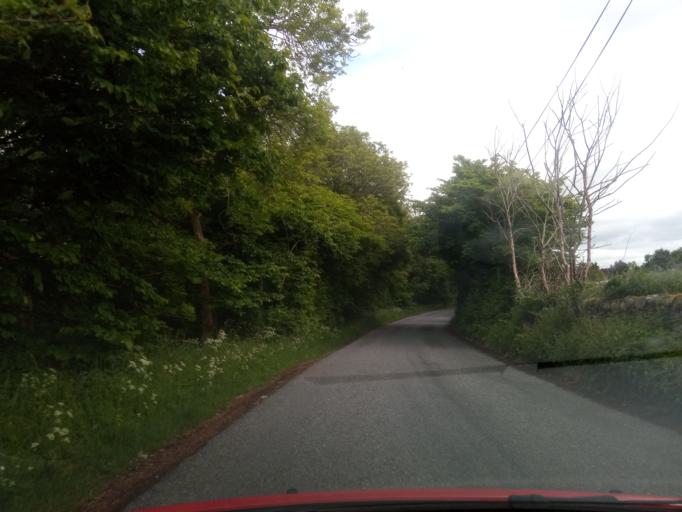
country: GB
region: Scotland
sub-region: The Scottish Borders
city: Selkirk
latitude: 55.5446
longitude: -2.8536
